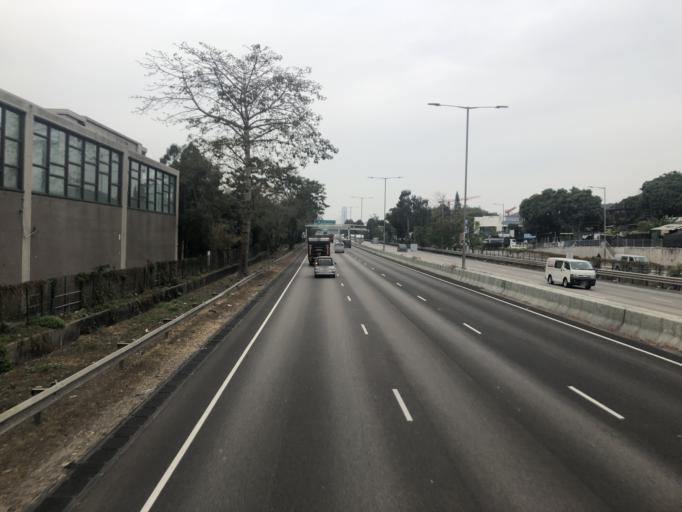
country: CN
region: Guangdong
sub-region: Shenzhen
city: Shenzhen
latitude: 22.5032
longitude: 114.1026
